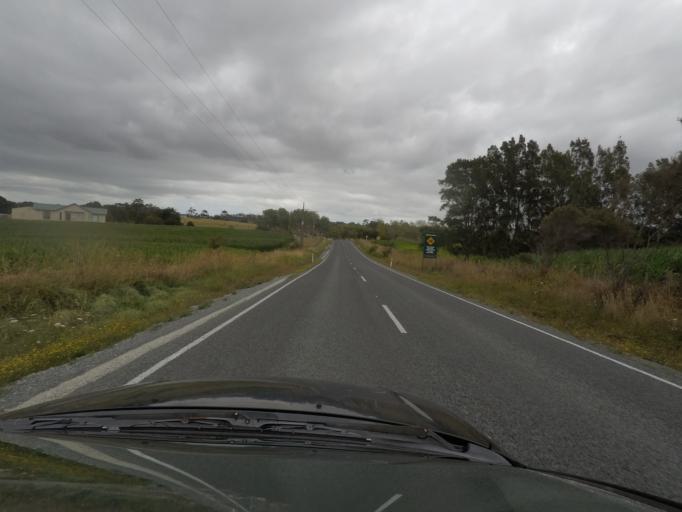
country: NZ
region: Auckland
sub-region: Auckland
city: Wellsford
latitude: -36.2820
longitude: 174.5686
